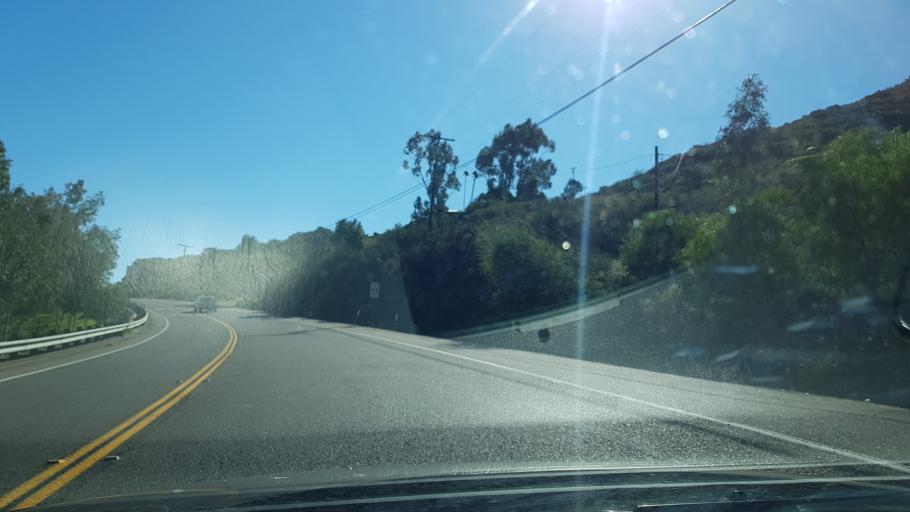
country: US
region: California
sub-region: San Diego County
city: Escondido
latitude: 33.0604
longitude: -117.1245
